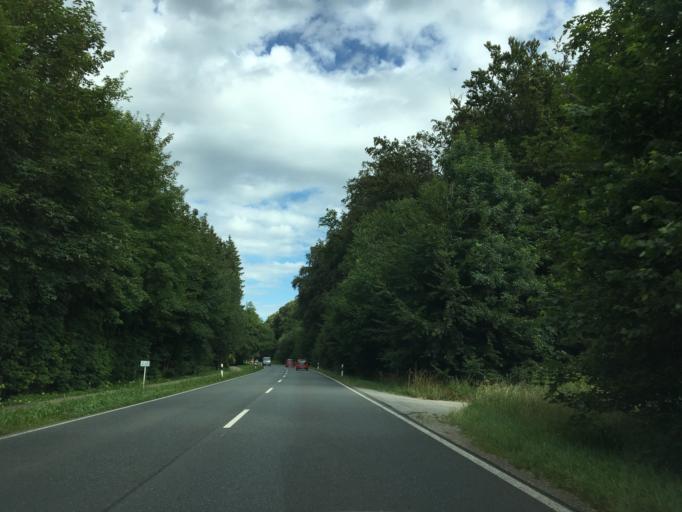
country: DE
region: Bavaria
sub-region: Upper Bavaria
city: Otterfing
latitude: 47.9204
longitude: 11.6660
